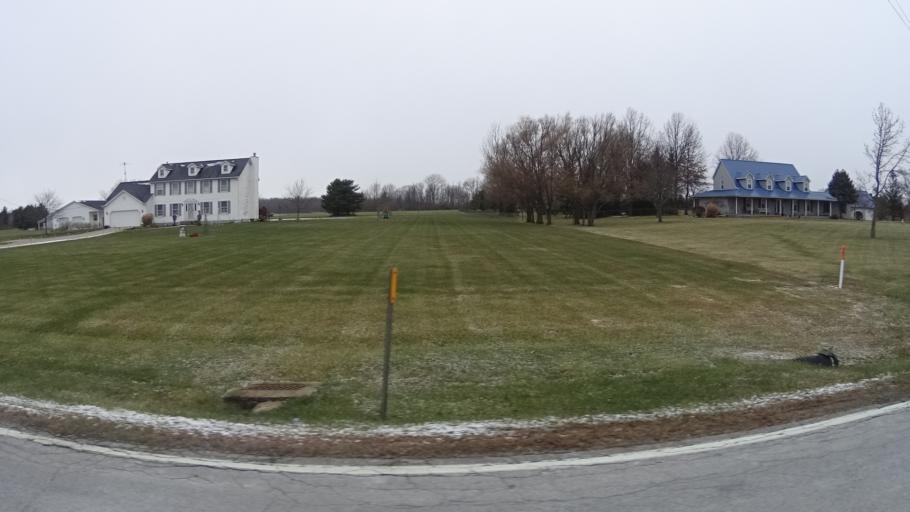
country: US
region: Ohio
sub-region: Lorain County
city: Lagrange
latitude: 41.1970
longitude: -82.1396
